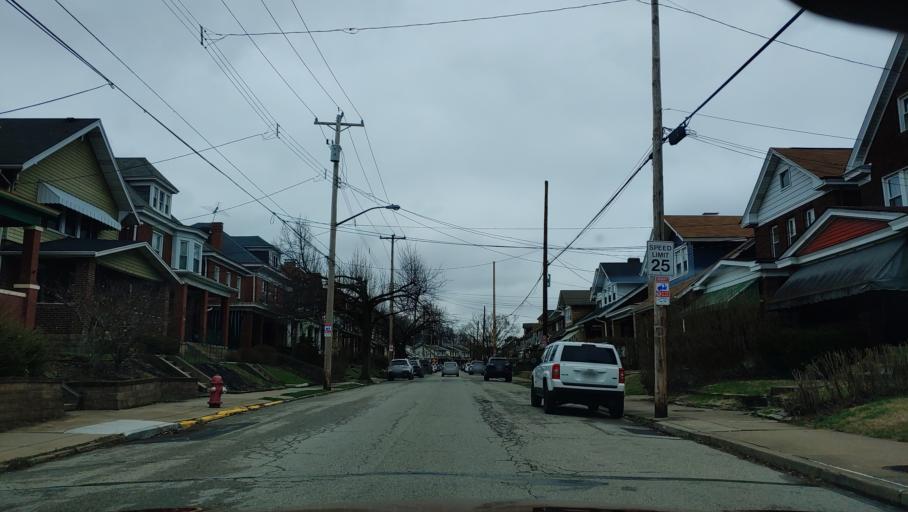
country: US
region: Pennsylvania
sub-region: Allegheny County
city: Sharpsburg
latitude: 40.4824
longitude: -79.9278
